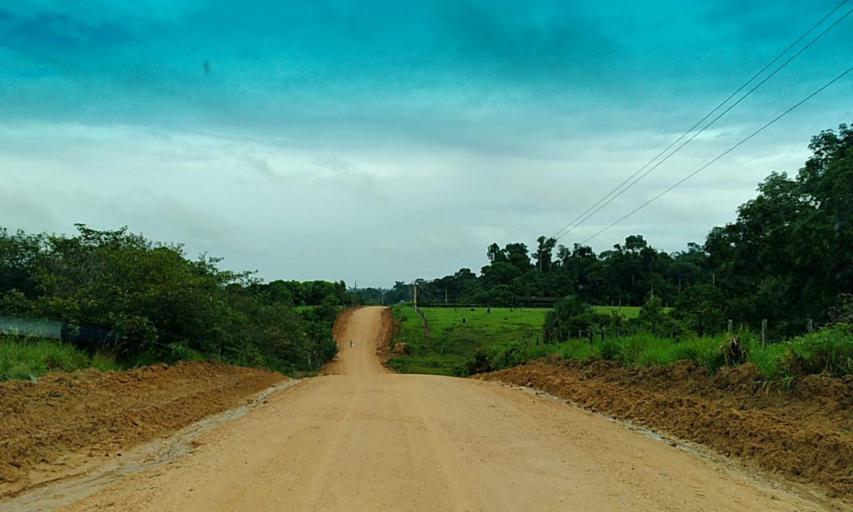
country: BR
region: Para
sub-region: Senador Jose Porfirio
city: Senador Jose Porfirio
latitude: -3.0239
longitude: -51.6811
